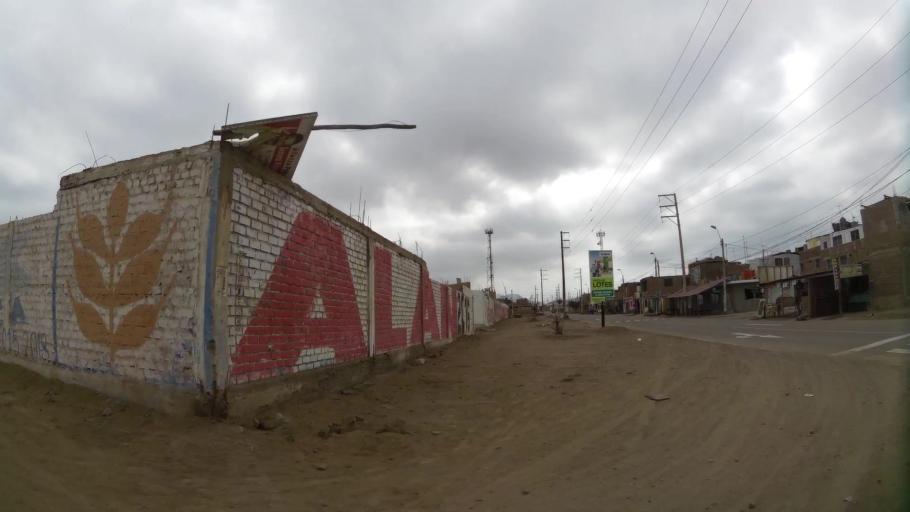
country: PE
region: Lima
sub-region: Provincia de Canete
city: Chilca
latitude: -12.5145
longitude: -76.7388
